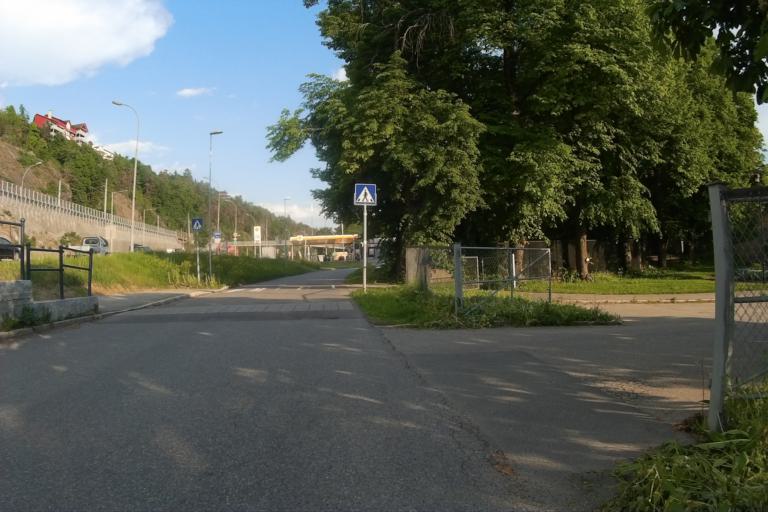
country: NO
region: Oslo
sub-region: Oslo
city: Oslo
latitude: 59.8815
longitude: 10.7721
